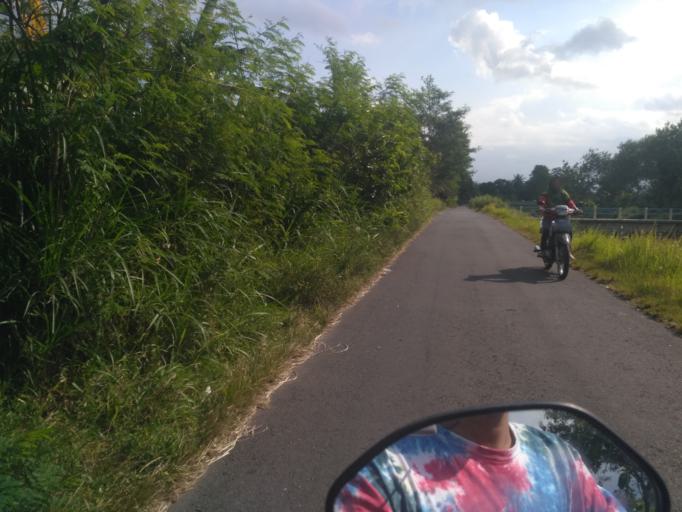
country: ID
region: Daerah Istimewa Yogyakarta
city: Godean
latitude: -7.7422
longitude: 110.3160
